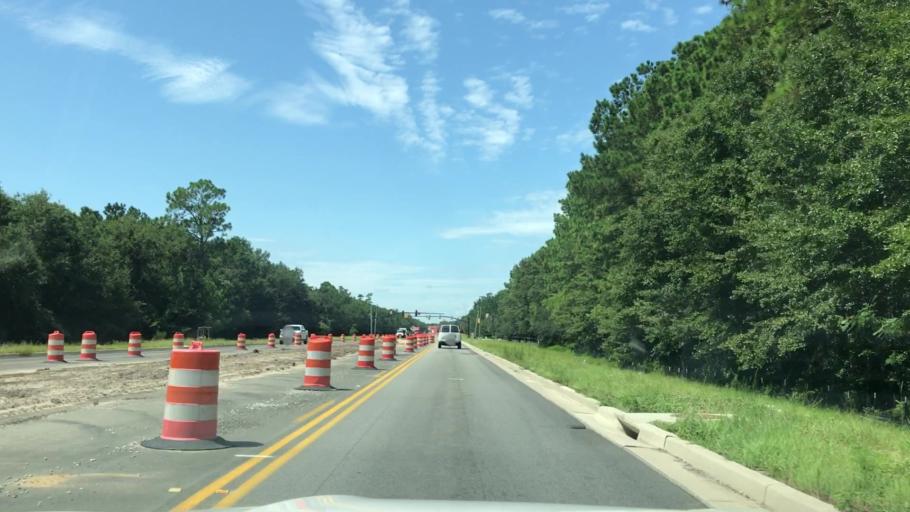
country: US
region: South Carolina
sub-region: Charleston County
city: North Charleston
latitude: 32.9085
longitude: -79.9020
